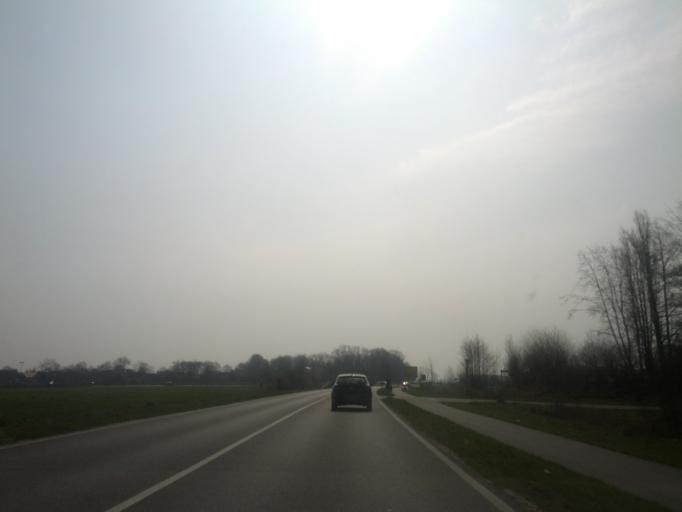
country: DE
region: Lower Saxony
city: Lutetsburg
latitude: 53.6010
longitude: 7.2345
